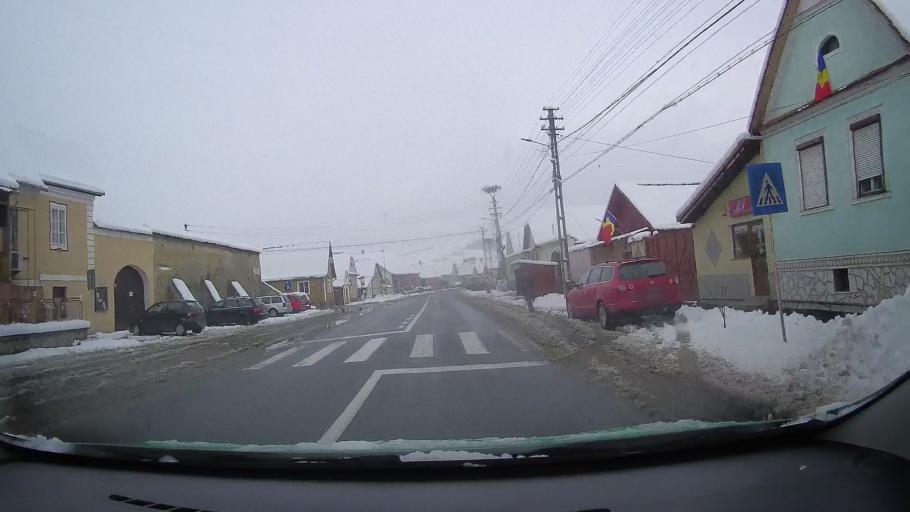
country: RO
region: Sibiu
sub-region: Comuna Cristian
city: Cristian
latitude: 45.7851
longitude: 24.0291
